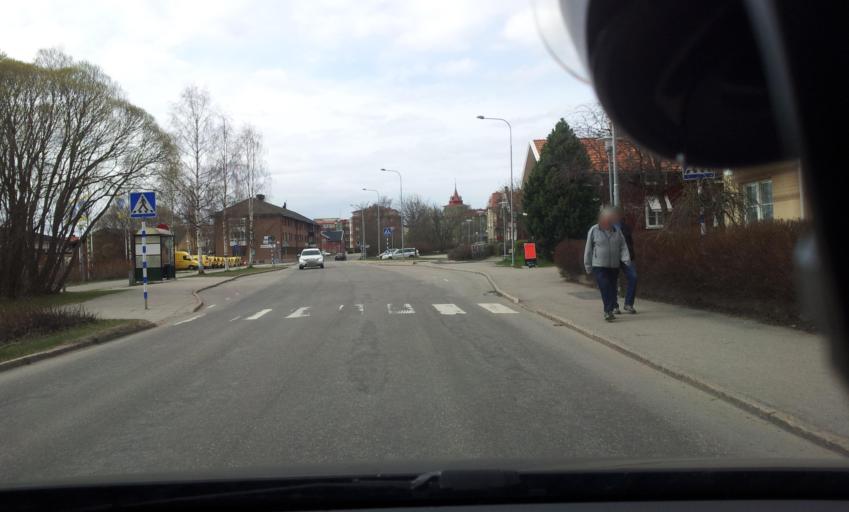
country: SE
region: Gaevleborg
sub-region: Ljusdals Kommun
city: Ljusdal
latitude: 61.8288
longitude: 16.0970
